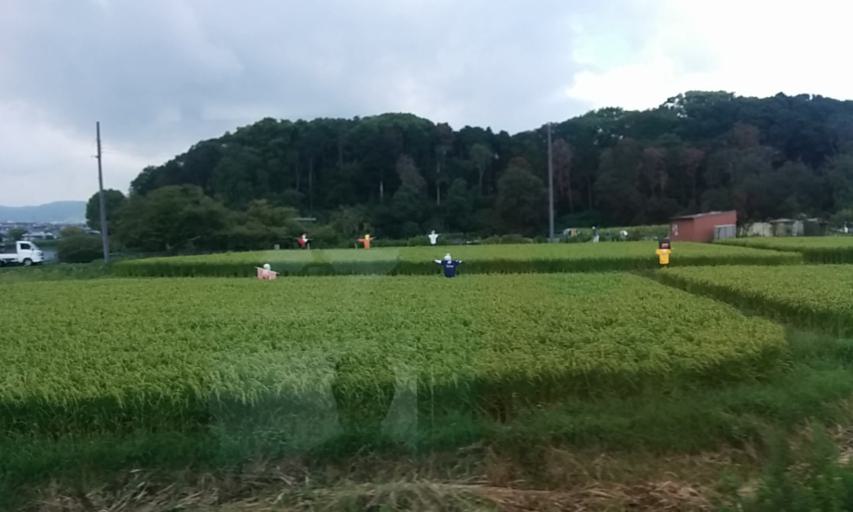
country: JP
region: Nara
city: Nara-shi
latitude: 34.6801
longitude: 135.7837
